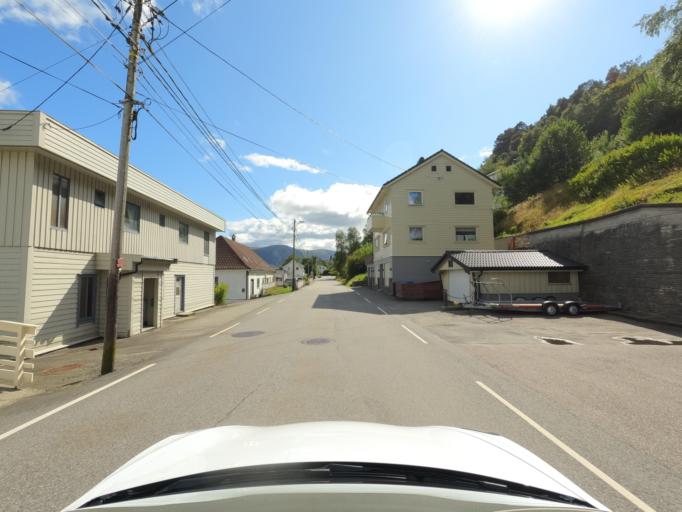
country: NO
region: Hordaland
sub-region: Bergen
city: Ytre Arna
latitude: 60.4548
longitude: 5.4448
